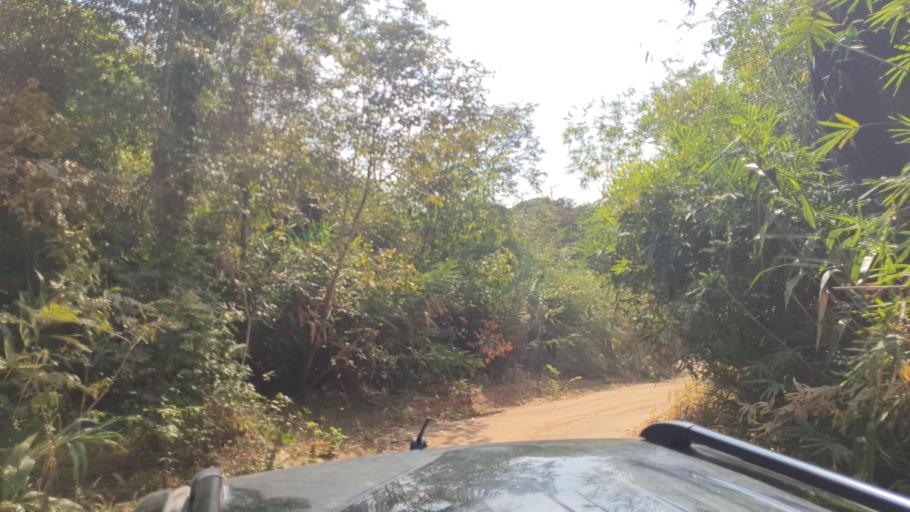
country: TH
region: Changwat Bueng Kan
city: Si Wilai
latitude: 18.2693
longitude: 103.7996
